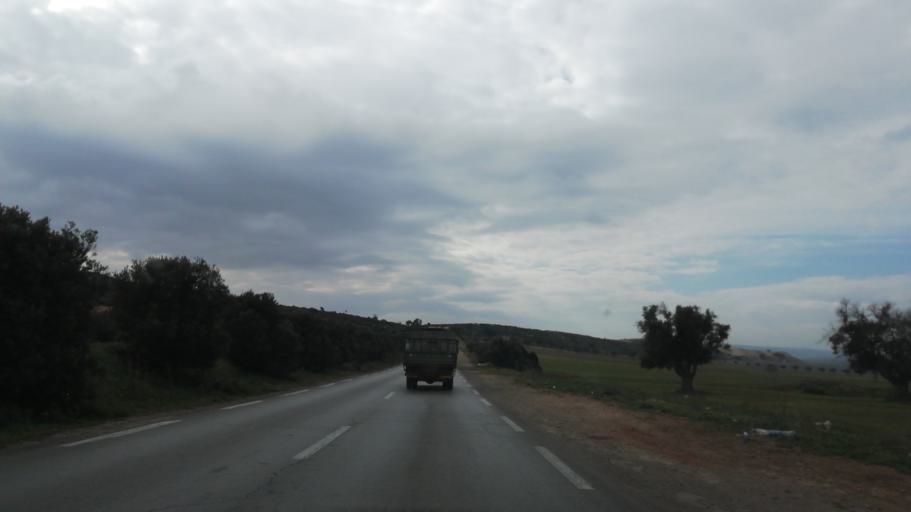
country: DZ
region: Oran
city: Ain el Bya
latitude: 35.7237
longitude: -0.3564
